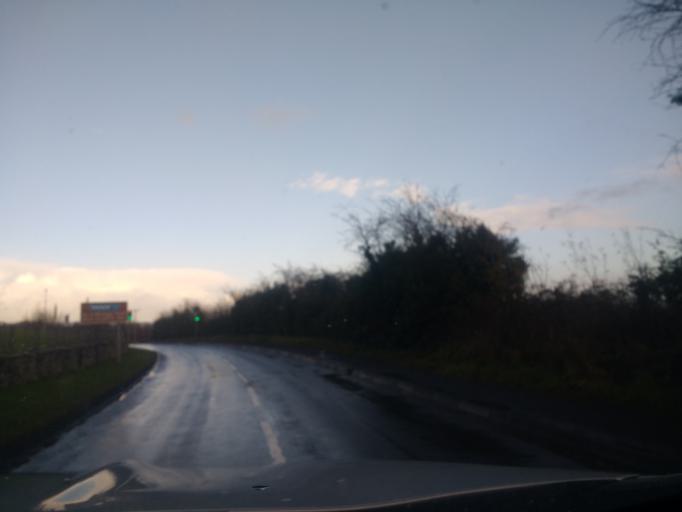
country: IE
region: Ulster
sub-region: County Donegal
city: Ramelton
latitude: 55.0387
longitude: -7.6473
